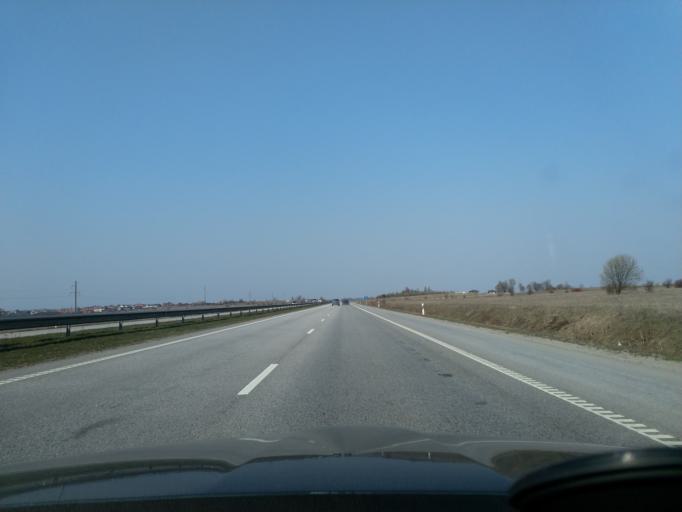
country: LT
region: Klaipedos apskritis
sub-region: Klaipeda
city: Klaipeda
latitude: 55.7379
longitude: 21.1809
